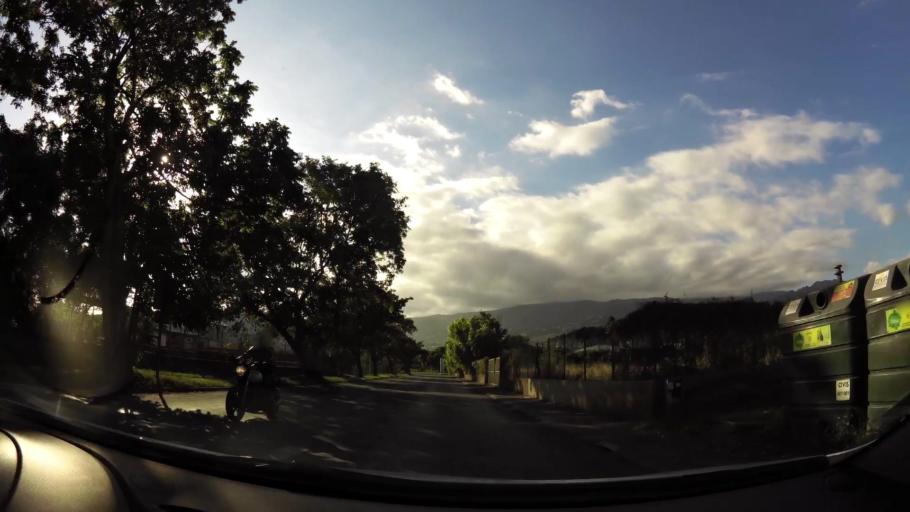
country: RE
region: Reunion
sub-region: Reunion
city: Saint-Louis
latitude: -21.2766
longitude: 55.3731
